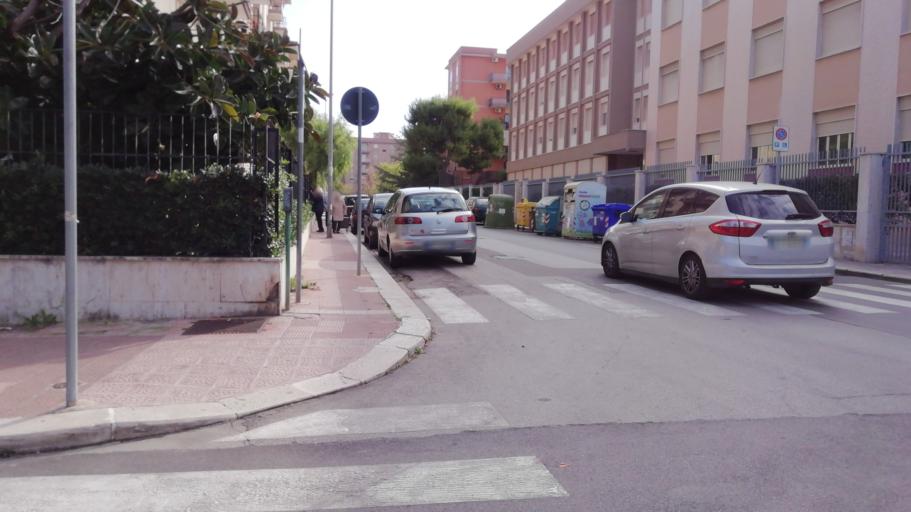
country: IT
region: Apulia
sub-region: Provincia di Bari
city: Bari
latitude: 41.1132
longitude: 16.8901
